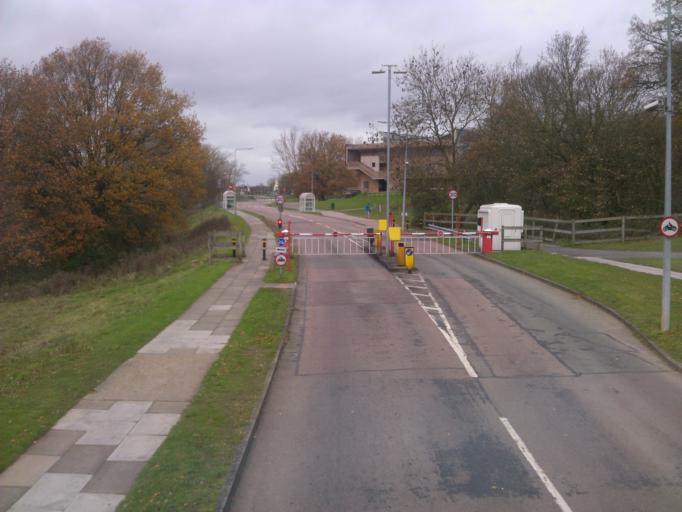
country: GB
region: England
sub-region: Essex
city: Rowhedge
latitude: 51.8769
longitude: 0.9420
